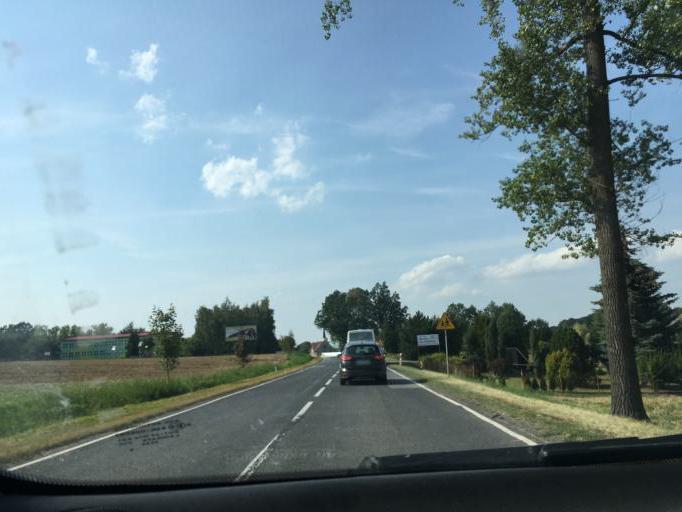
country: PL
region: Opole Voivodeship
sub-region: Powiat prudnicki
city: Laka Prudnicka
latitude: 50.3790
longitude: 17.5310
